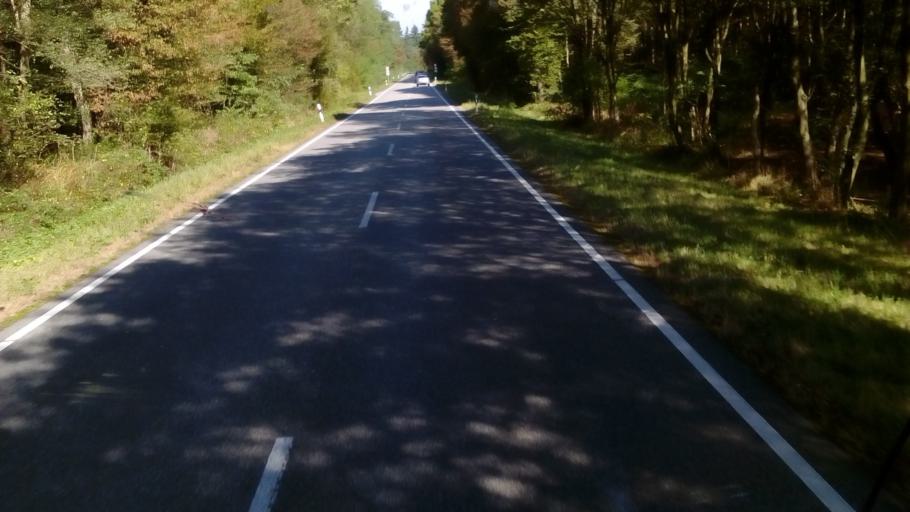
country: DE
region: Rheinland-Pfalz
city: Berg
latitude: 49.0010
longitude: 8.1817
